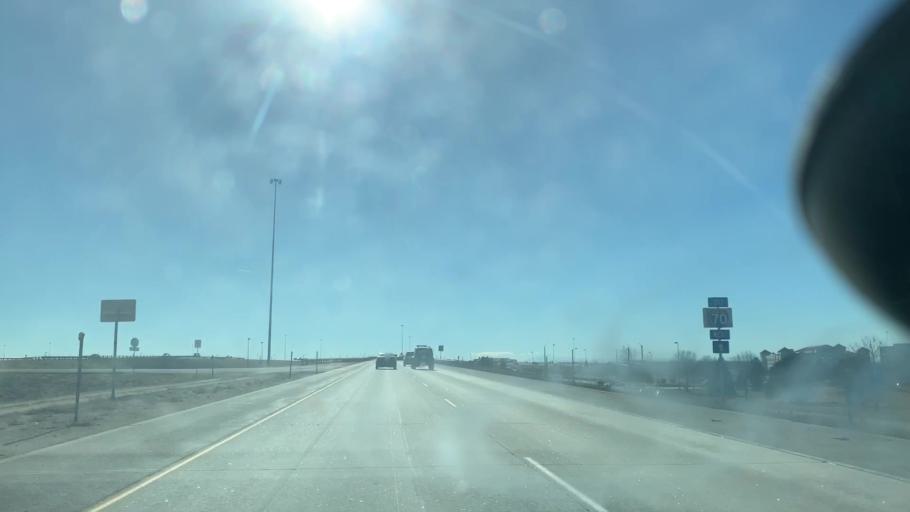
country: US
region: Colorado
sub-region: Adams County
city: Aurora
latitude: 39.7748
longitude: -104.7915
